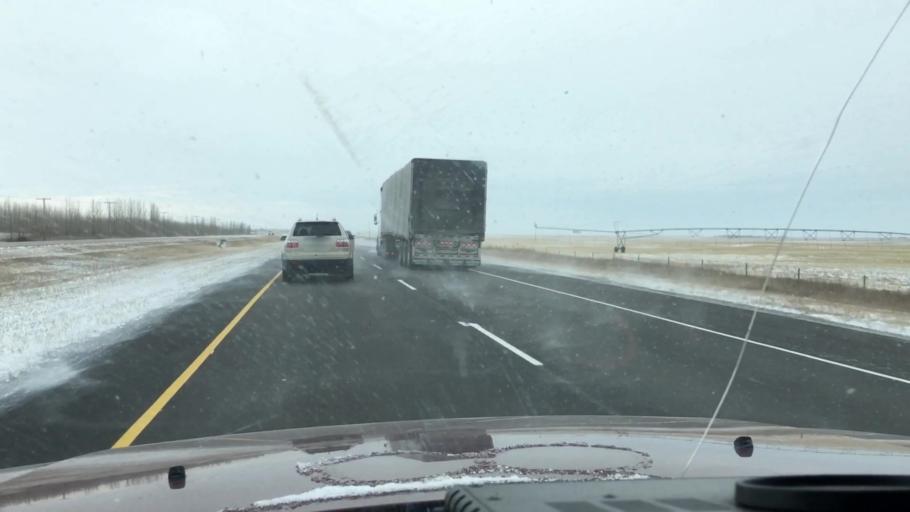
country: CA
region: Saskatchewan
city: Saskatoon
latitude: 51.7738
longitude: -106.4763
